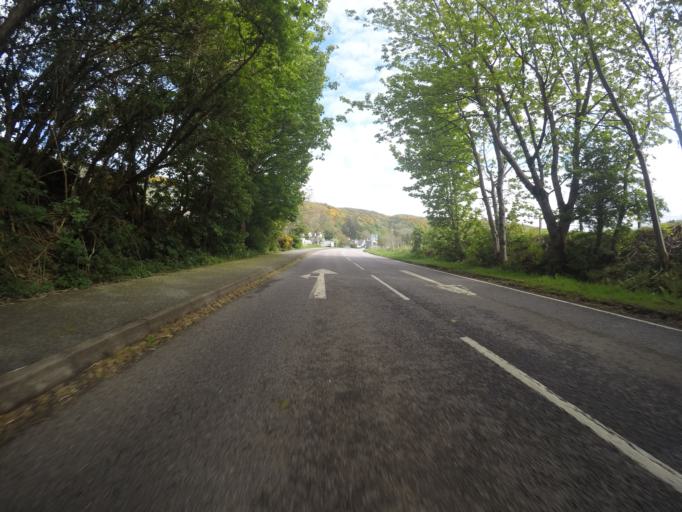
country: GB
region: Scotland
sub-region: Highland
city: Portree
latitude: 57.5916
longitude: -6.3603
